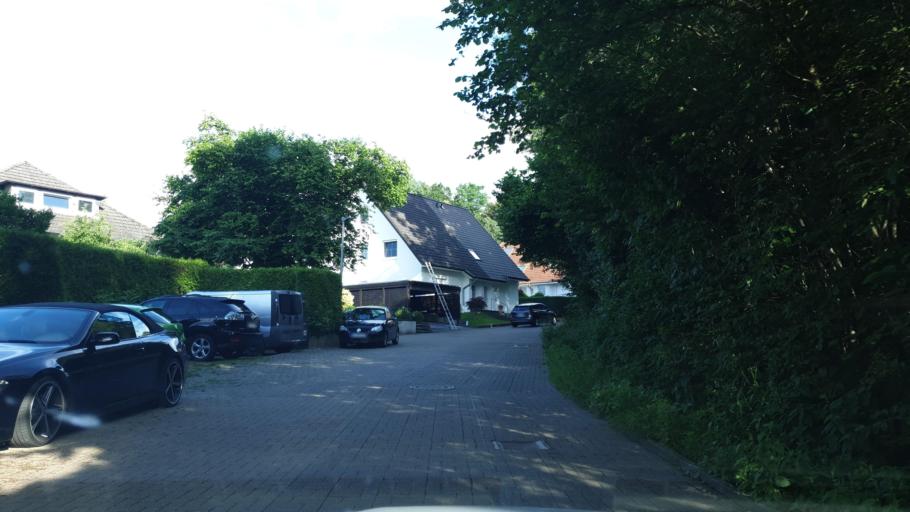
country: DE
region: North Rhine-Westphalia
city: Bad Oeynhausen
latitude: 52.1857
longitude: 8.7927
